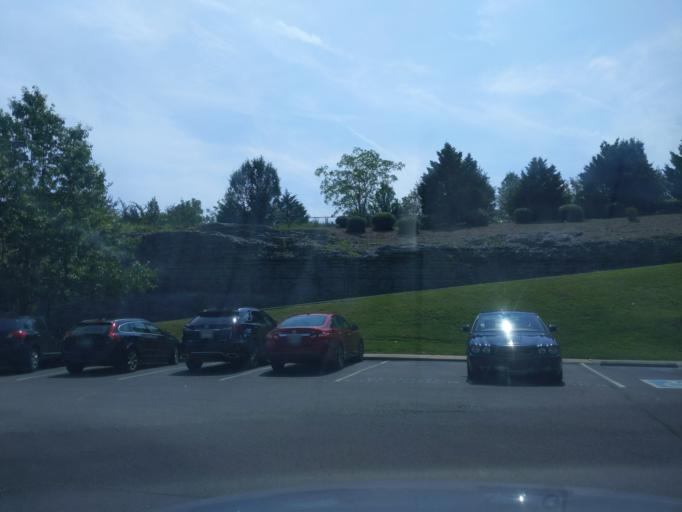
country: US
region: Tennessee
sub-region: Williamson County
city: Brentwood Estates
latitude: 36.0400
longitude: -86.7465
